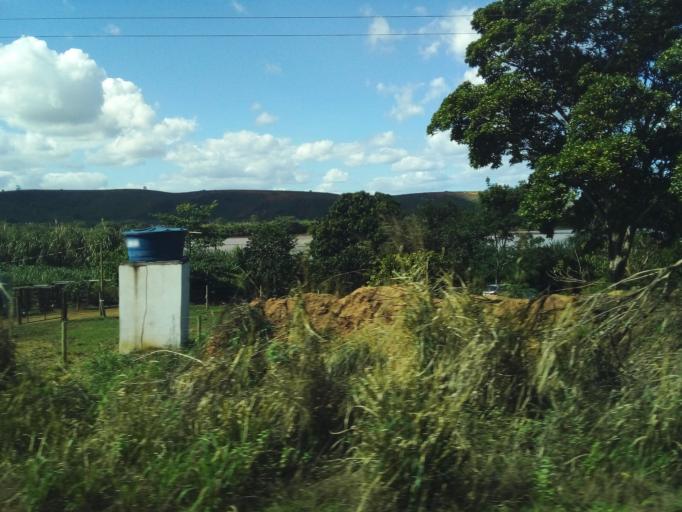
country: BR
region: Minas Gerais
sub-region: Governador Valadares
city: Governador Valadares
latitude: -18.8705
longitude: -41.7675
